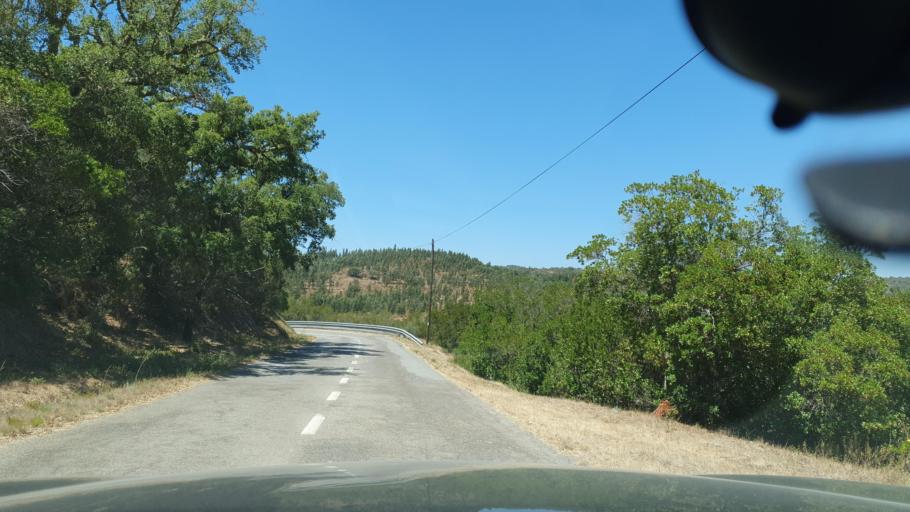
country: PT
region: Beja
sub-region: Odemira
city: Odemira
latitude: 37.6017
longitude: -8.5704
